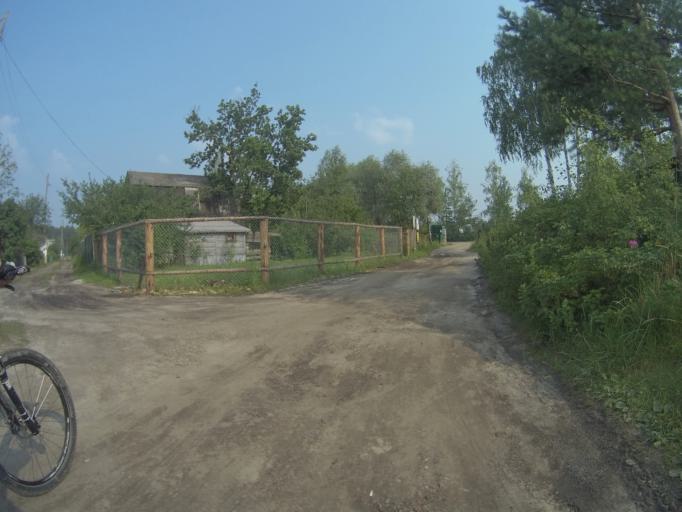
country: RU
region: Vladimir
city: Vorsha
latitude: 56.0113
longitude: 40.1313
